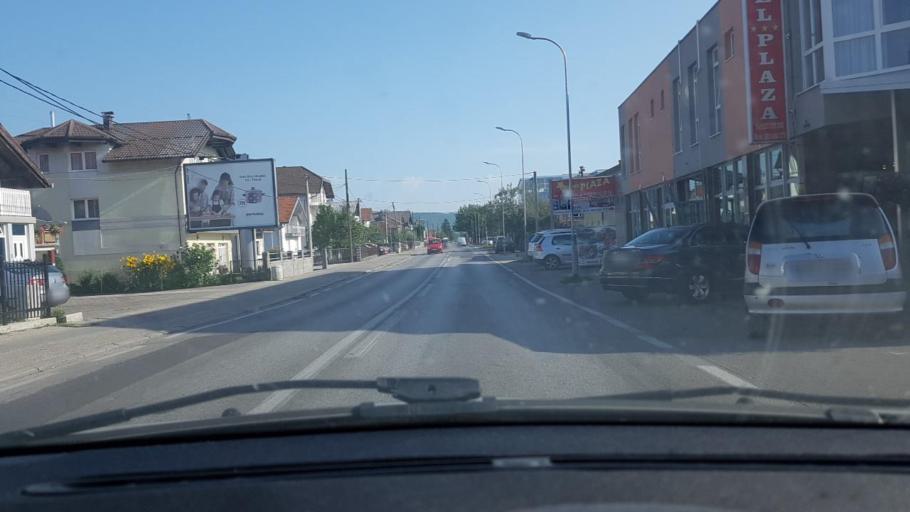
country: BA
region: Federation of Bosnia and Herzegovina
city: Bihac
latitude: 44.8240
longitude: 15.8817
